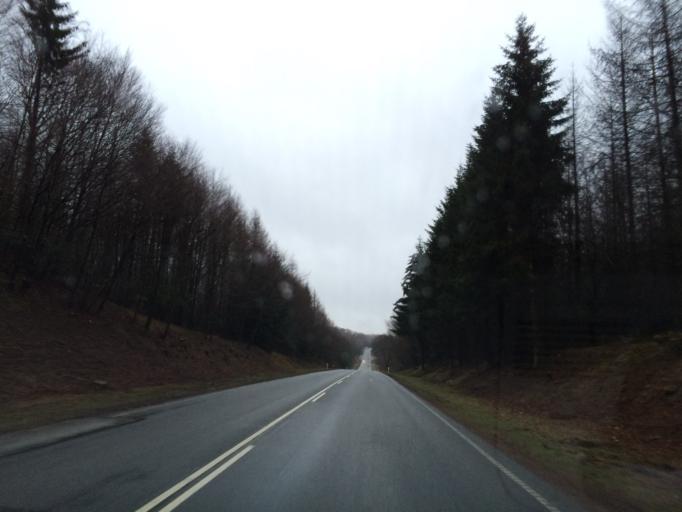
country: DK
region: North Denmark
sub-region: Mariagerfjord Kommune
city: Arden
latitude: 56.8008
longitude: 9.8177
